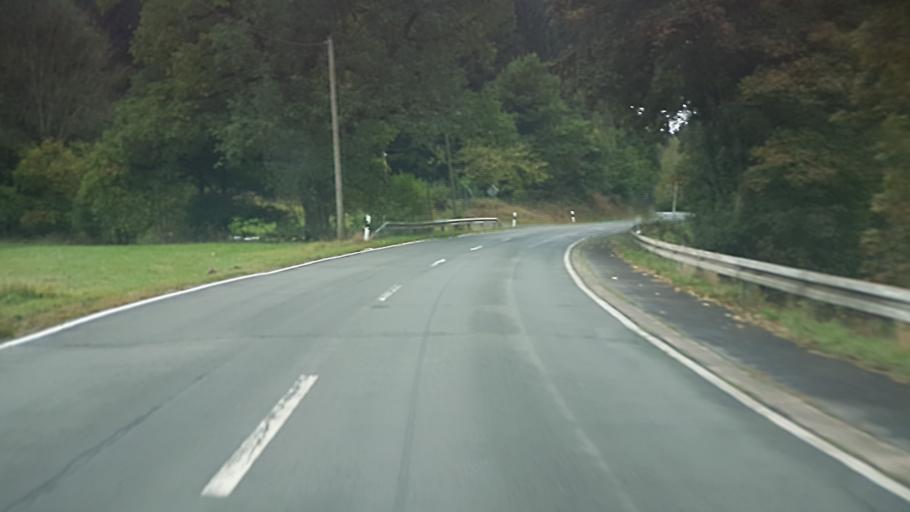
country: DE
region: North Rhine-Westphalia
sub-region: Regierungsbezirk Arnsberg
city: Herscheid
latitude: 51.2093
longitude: 7.6953
